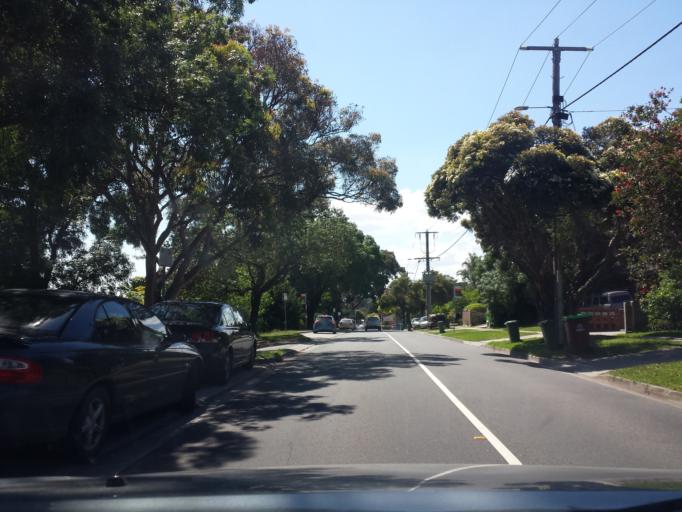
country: AU
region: Victoria
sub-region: Casey
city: Berwick
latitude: -38.0370
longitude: 145.3440
